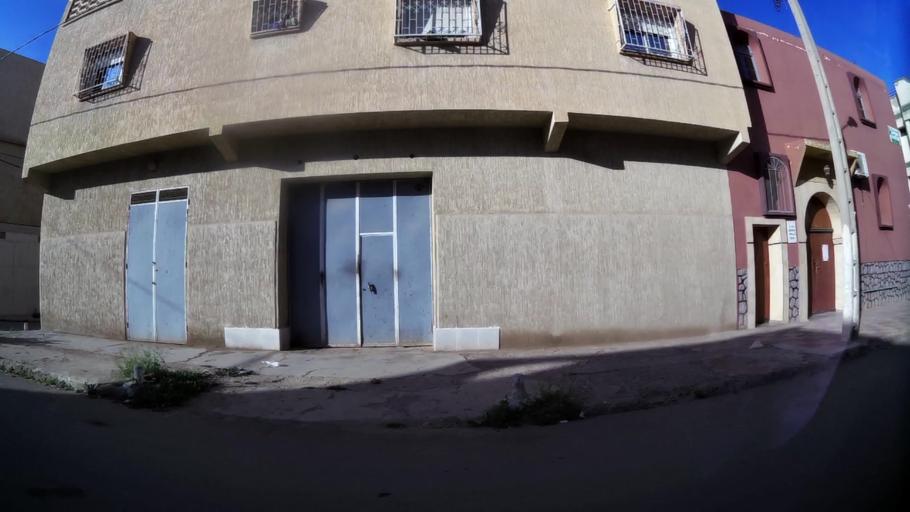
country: MA
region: Oriental
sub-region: Oujda-Angad
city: Oujda
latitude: 34.6939
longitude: -1.9148
